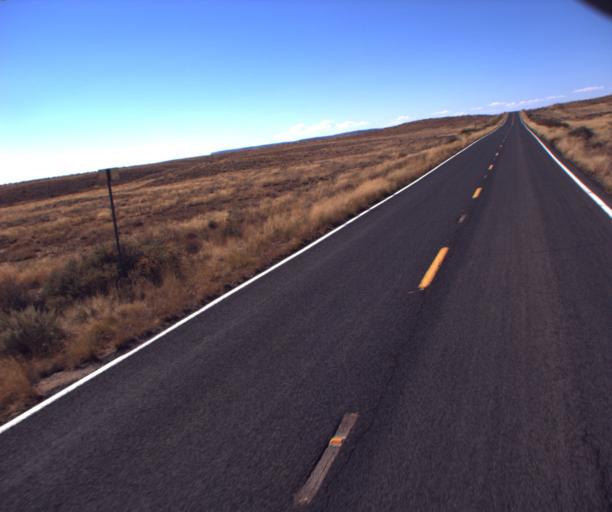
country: US
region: Arizona
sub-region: Navajo County
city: First Mesa
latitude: 35.9775
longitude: -110.7506
